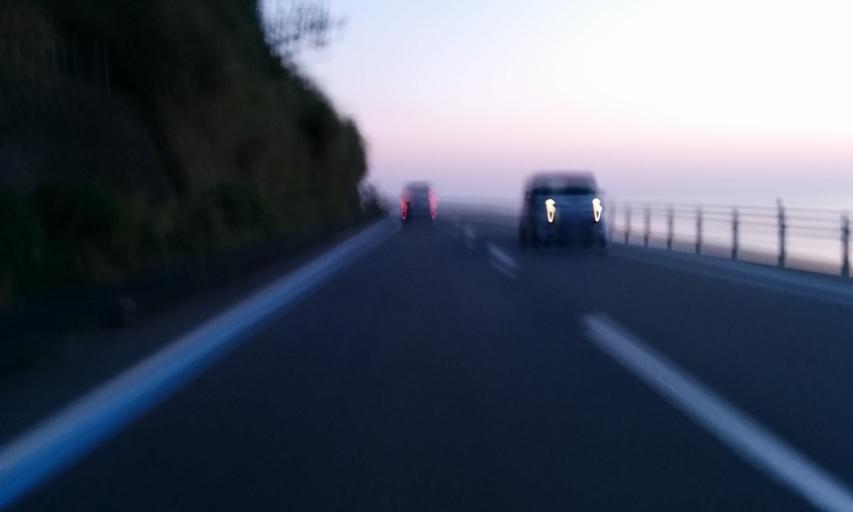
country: JP
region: Ehime
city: Ozu
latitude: 33.5863
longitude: 132.4532
